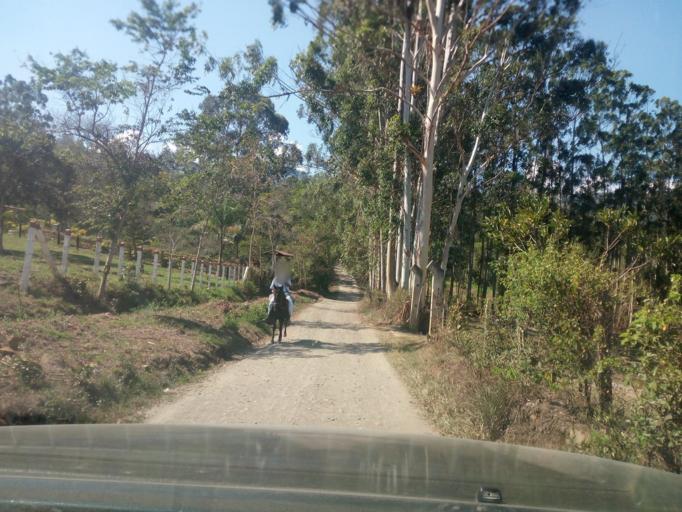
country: CO
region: Boyaca
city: Guateque
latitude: 4.9948
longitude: -73.4645
